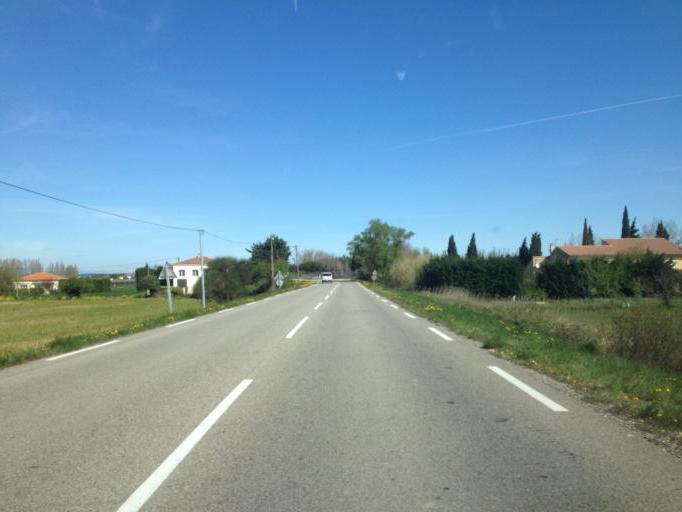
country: FR
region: Provence-Alpes-Cote d'Azur
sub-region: Departement du Vaucluse
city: Orange
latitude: 44.1349
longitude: 4.7819
